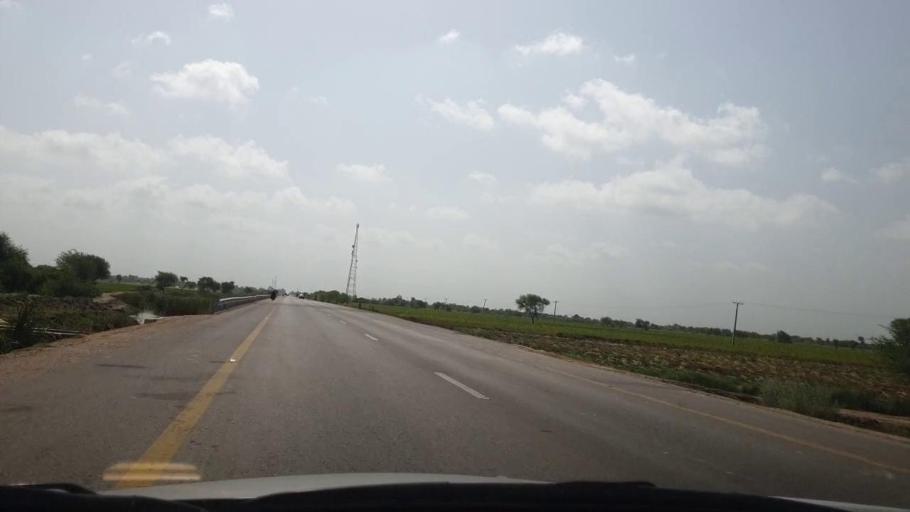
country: PK
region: Sindh
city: Matli
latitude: 24.9569
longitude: 68.6882
